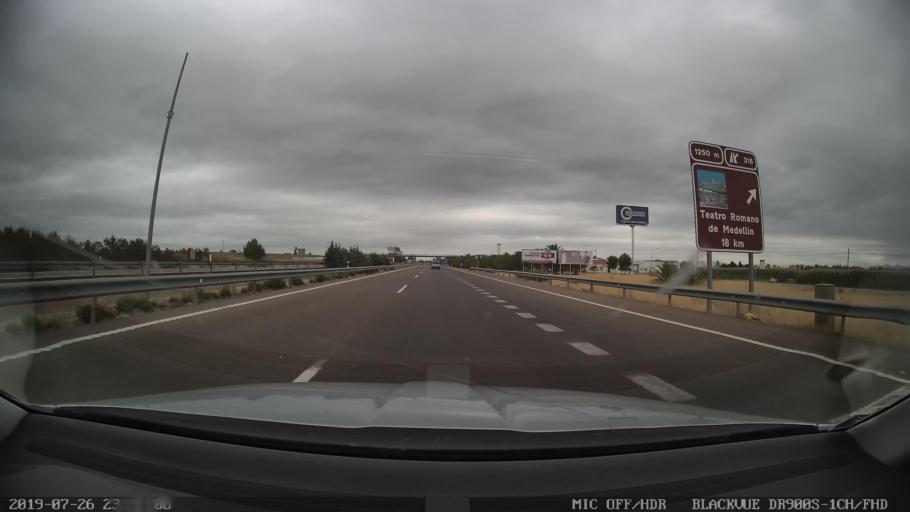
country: ES
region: Extremadura
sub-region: Provincia de Badajoz
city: San Pedro de Merida
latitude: 38.9910
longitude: -6.1167
